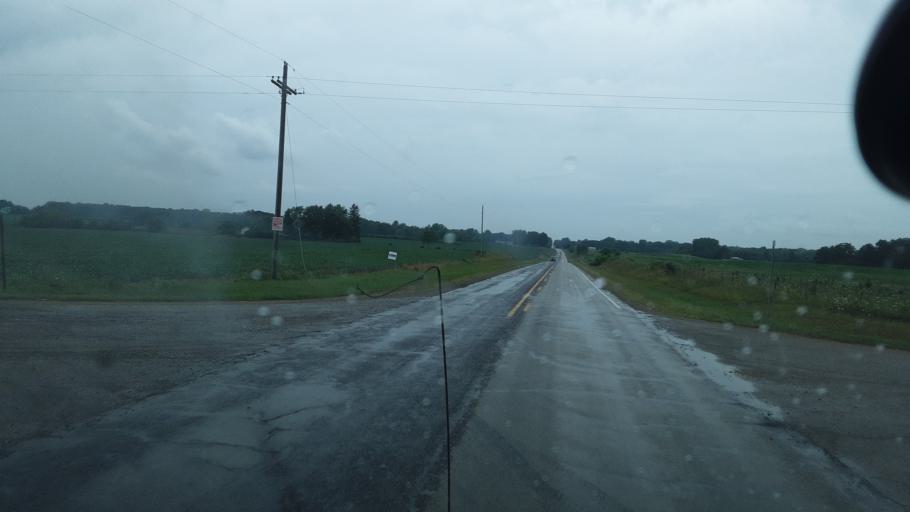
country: US
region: Indiana
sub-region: Steuben County
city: Hamilton
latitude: 41.5591
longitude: -84.8165
